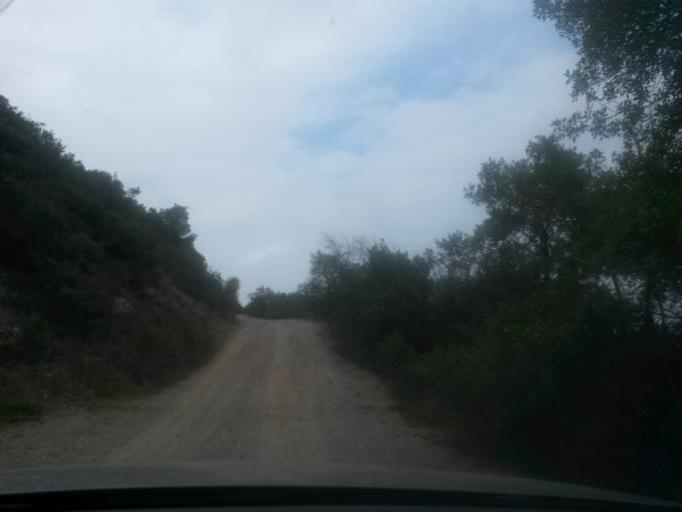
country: IT
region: Tuscany
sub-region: Provincia di Livorno
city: Porto Azzurro
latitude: 42.7422
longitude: 10.4098
